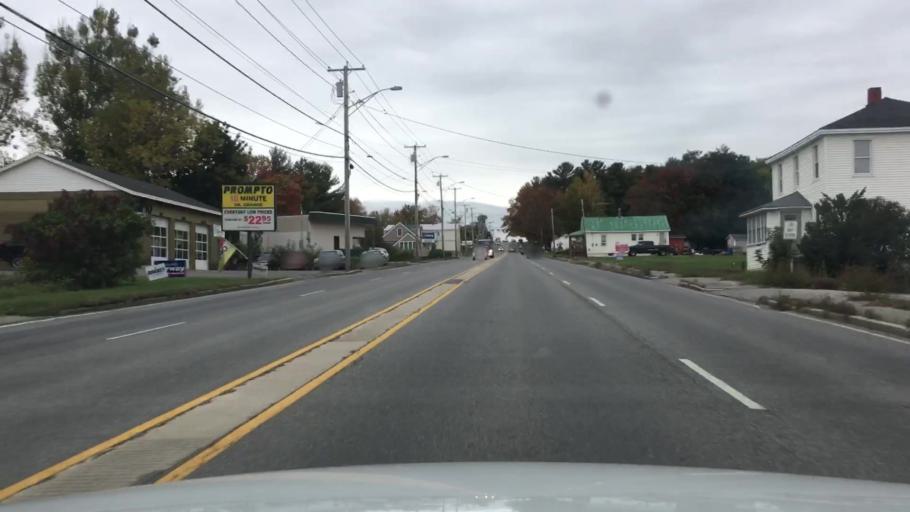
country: US
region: Maine
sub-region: Kennebec County
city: Waterville
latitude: 44.5418
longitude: -69.6557
